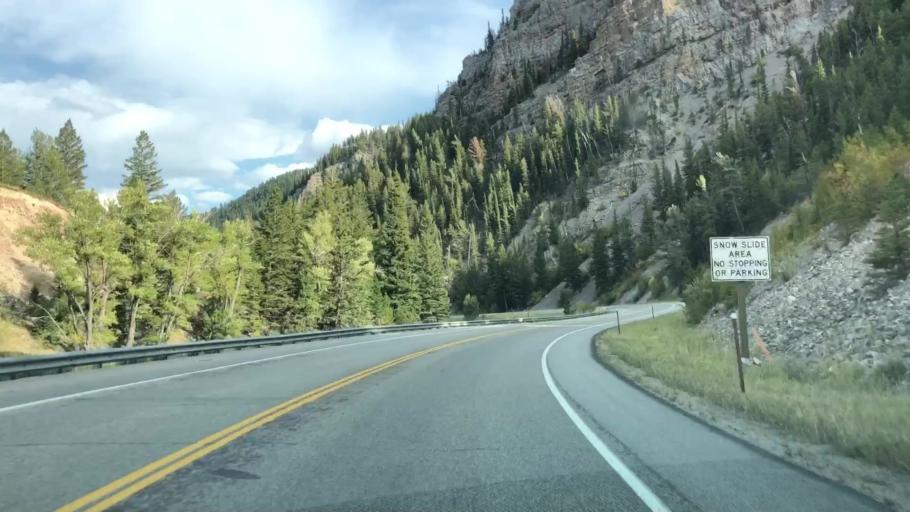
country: US
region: Wyoming
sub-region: Teton County
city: Hoback
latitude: 43.2828
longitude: -110.6189
